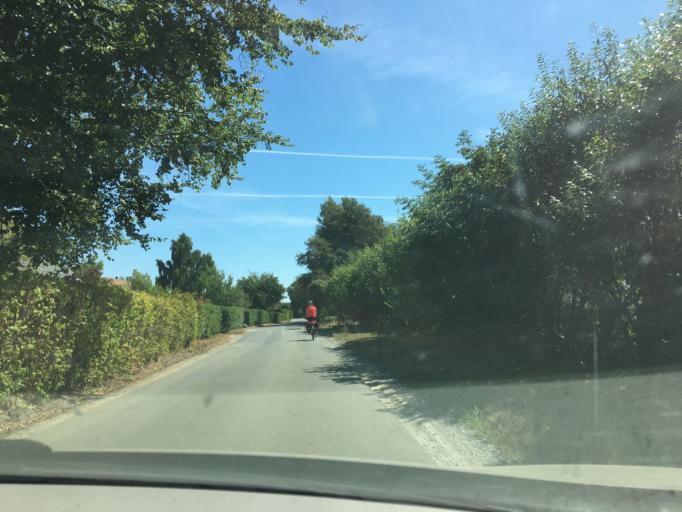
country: DK
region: South Denmark
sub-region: Middelfart Kommune
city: Norre Aby
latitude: 55.5153
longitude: 9.8509
